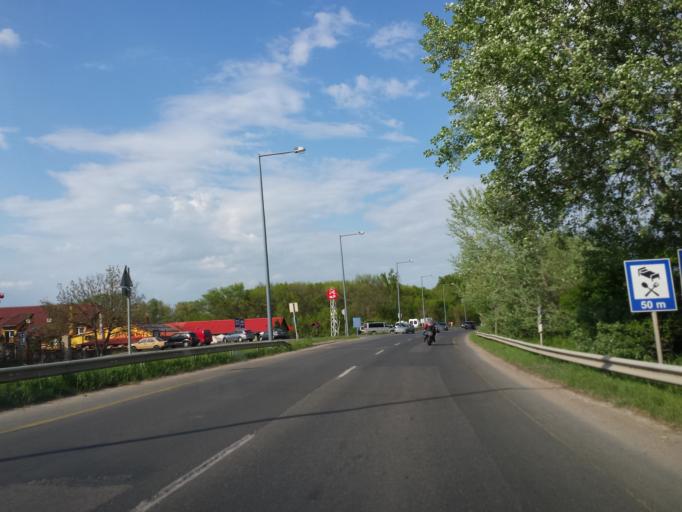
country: HU
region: Csongrad
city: Mako
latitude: 46.2060
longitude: 20.4557
